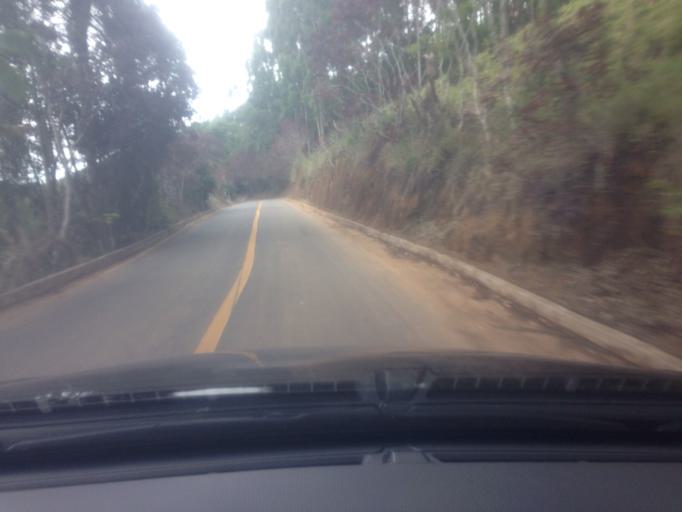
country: BR
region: Espirito Santo
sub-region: Guarapari
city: Guarapari
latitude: -20.5545
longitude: -40.5553
